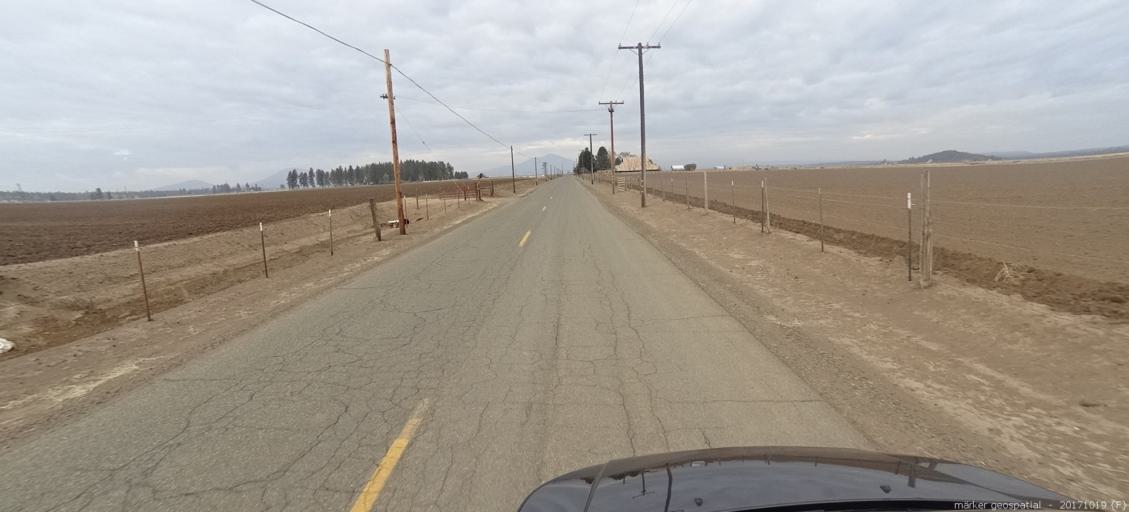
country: US
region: California
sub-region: Shasta County
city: Burney
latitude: 41.0806
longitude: -121.3416
